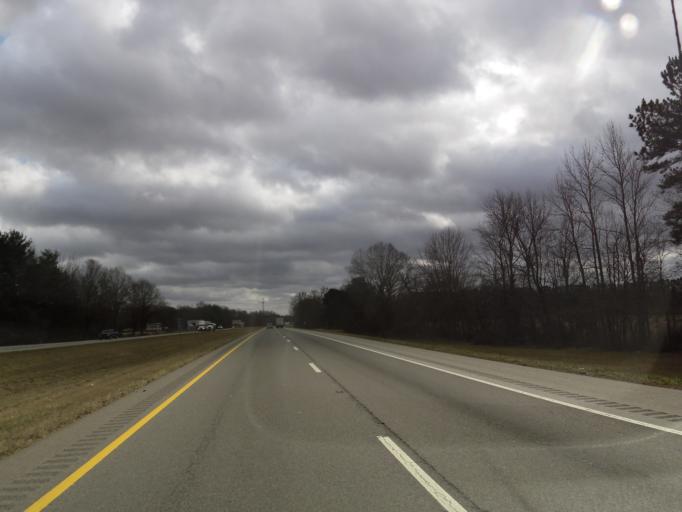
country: US
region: Tennessee
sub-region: Coffee County
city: Manchester
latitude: 35.4735
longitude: -86.0609
